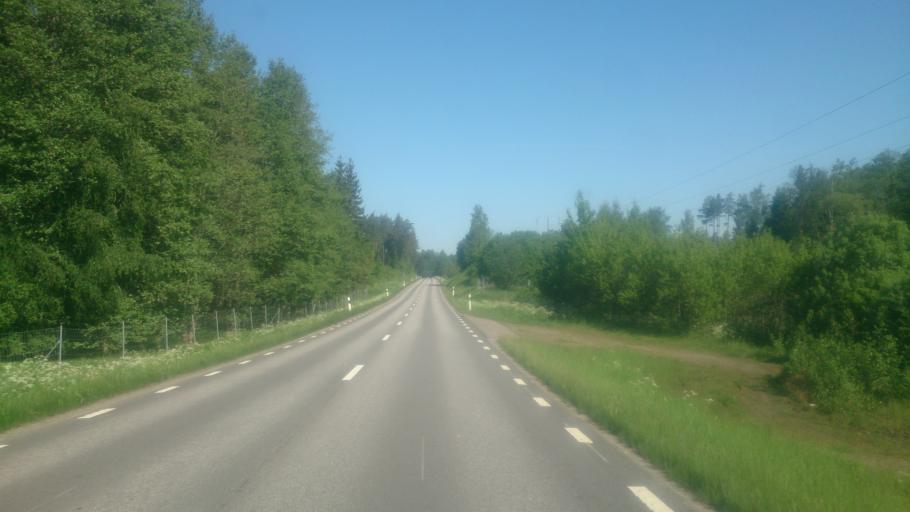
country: SE
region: OEstergoetland
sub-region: Atvidabergs Kommun
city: Atvidaberg
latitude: 58.1578
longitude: 16.0673
